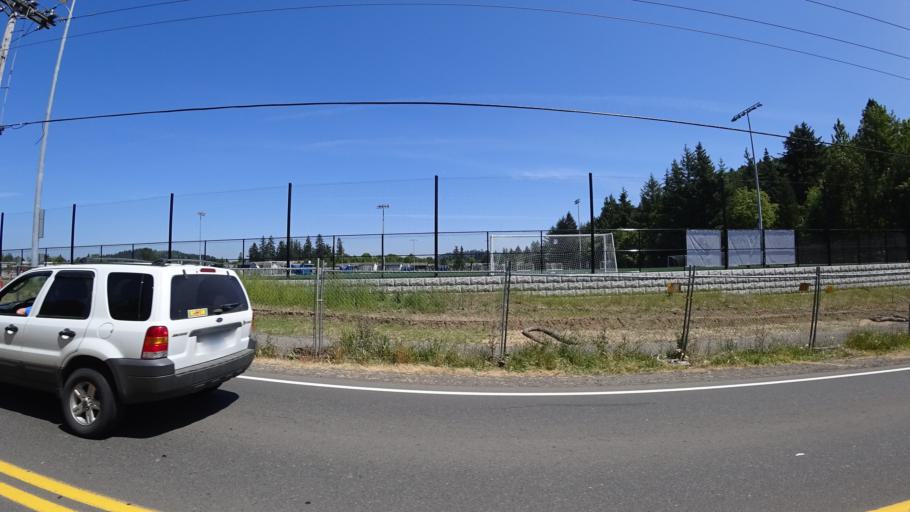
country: US
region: Oregon
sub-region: Multnomah County
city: Gresham
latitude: 45.4878
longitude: -122.4847
